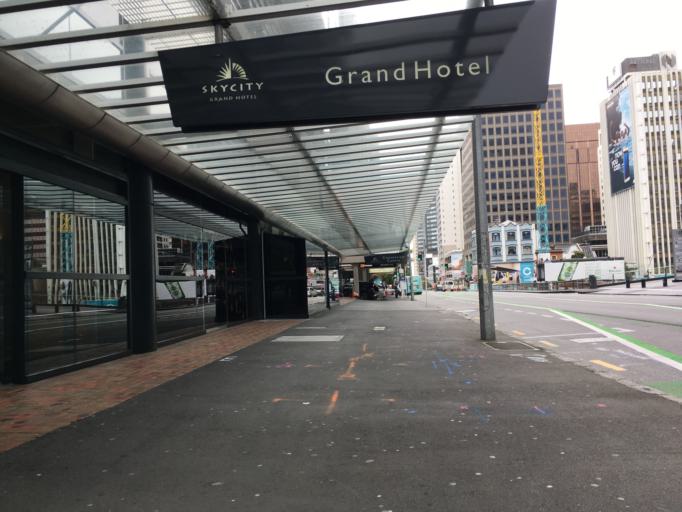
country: NZ
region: Auckland
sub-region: Auckland
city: Auckland
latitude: -36.8496
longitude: 174.7633
